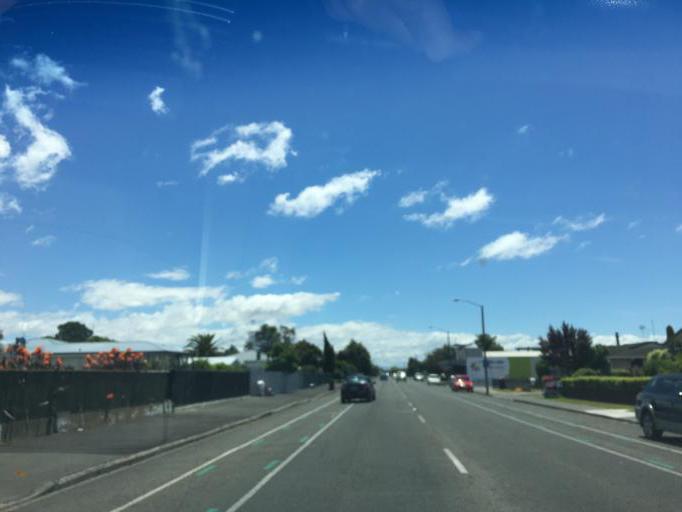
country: NZ
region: Hawke's Bay
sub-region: Hastings District
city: Hastings
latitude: -39.6472
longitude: 176.8542
